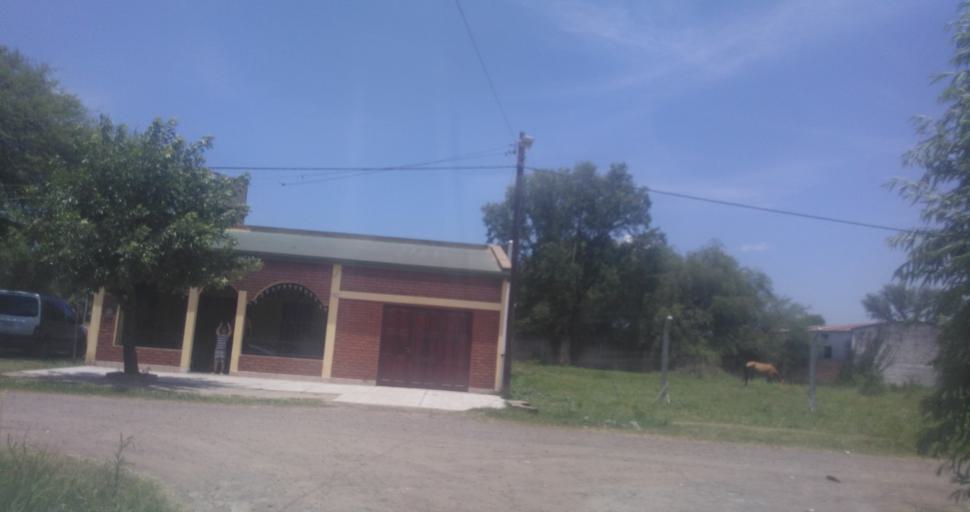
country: AR
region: Chaco
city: Fontana
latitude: -27.4226
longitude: -59.0357
